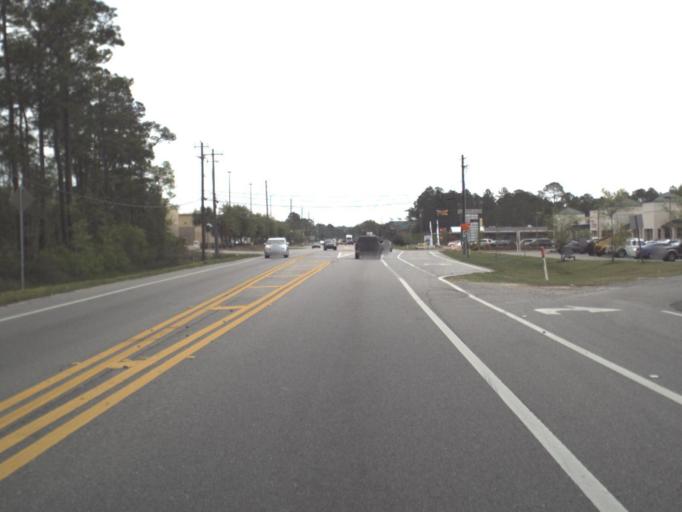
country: US
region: Florida
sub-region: Escambia County
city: Myrtle Grove
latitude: 30.3588
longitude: -87.3631
